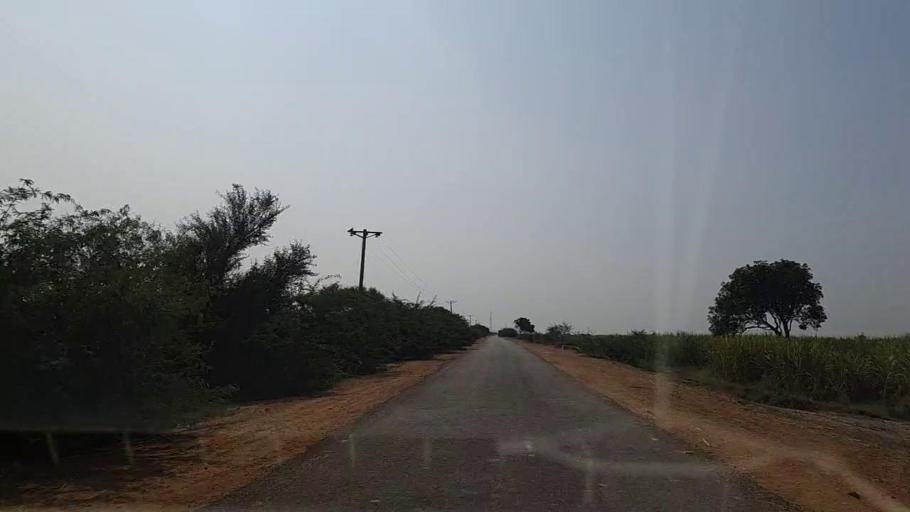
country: PK
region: Sindh
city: Chuhar Jamali
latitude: 24.2975
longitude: 67.9309
